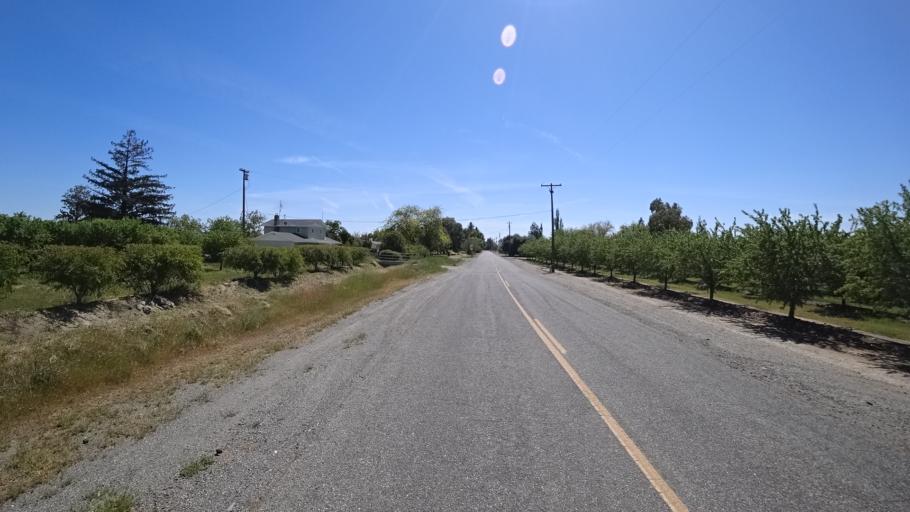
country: US
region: California
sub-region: Glenn County
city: Orland
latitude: 39.7393
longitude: -122.1594
